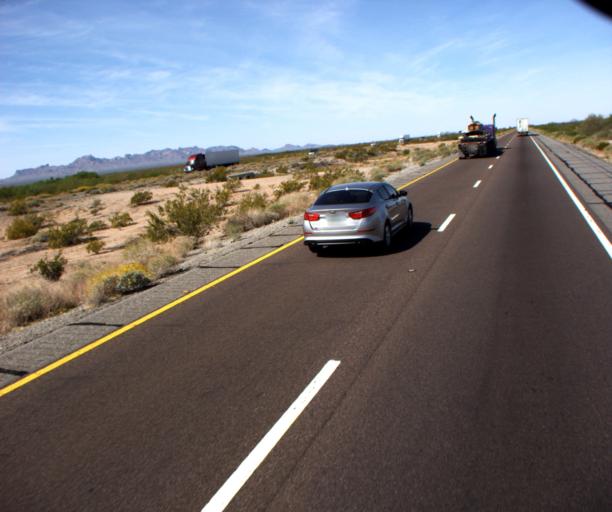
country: US
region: Arizona
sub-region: La Paz County
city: Salome
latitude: 33.5520
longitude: -113.2389
